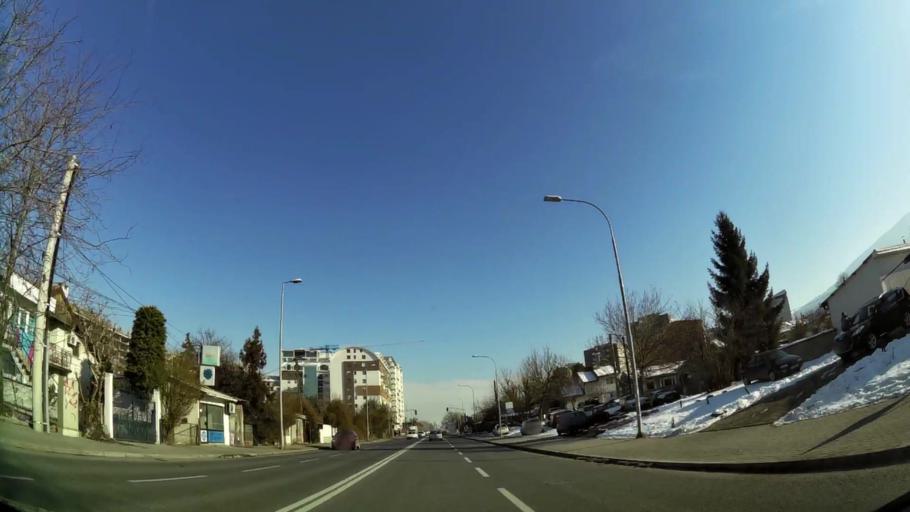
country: MK
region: Karpos
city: Skopje
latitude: 41.9977
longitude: 21.3951
